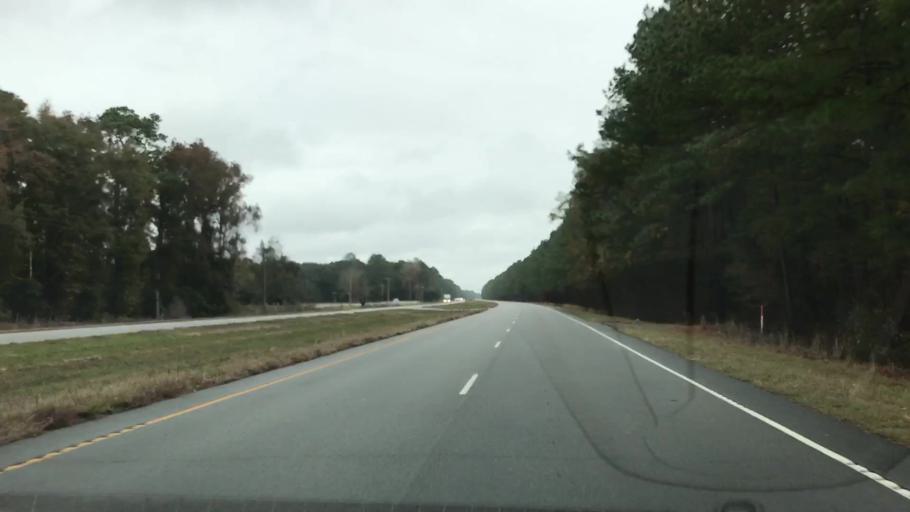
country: US
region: South Carolina
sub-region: Charleston County
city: Awendaw
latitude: 33.1221
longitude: -79.4518
